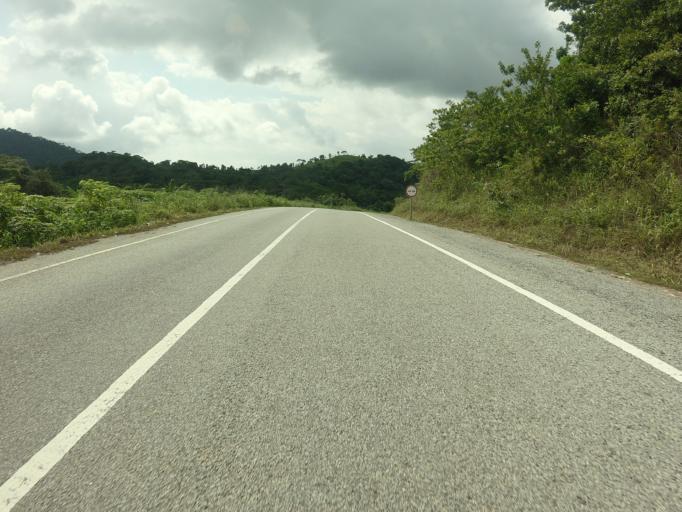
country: GH
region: Volta
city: Kpandu
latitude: 6.8294
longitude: 0.4176
